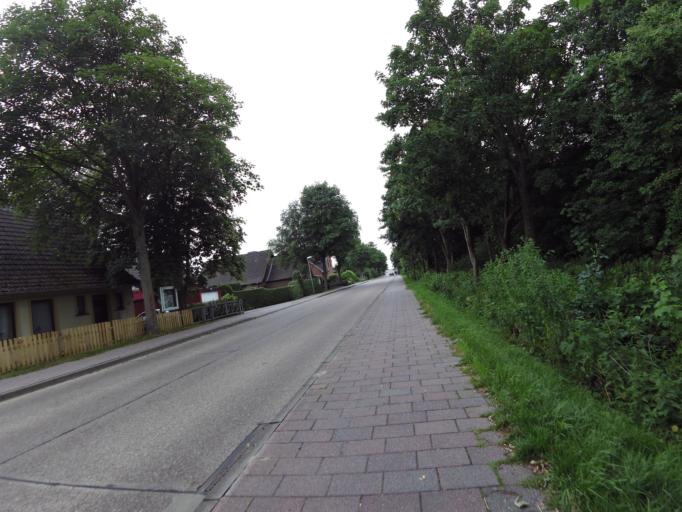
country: DE
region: Lower Saxony
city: Padingbuttel
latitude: 53.7344
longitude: 8.5231
